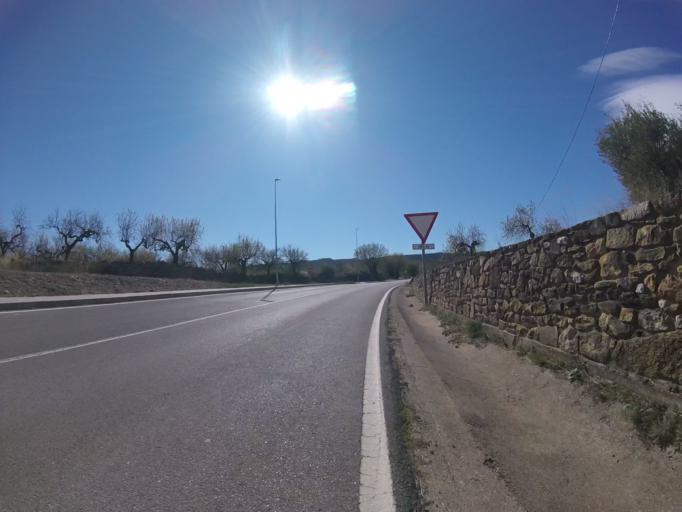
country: ES
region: Valencia
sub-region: Provincia de Castello
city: Albocasser
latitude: 40.3635
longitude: 0.0217
